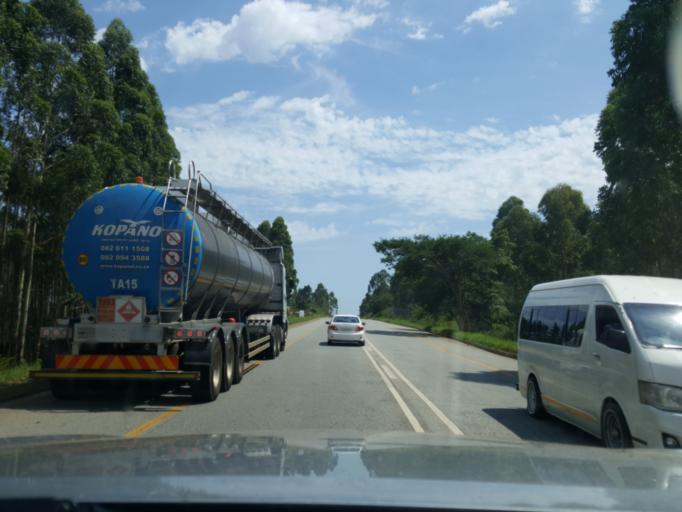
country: ZA
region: Mpumalanga
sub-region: Ehlanzeni District
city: White River
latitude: -25.2327
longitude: 31.0257
